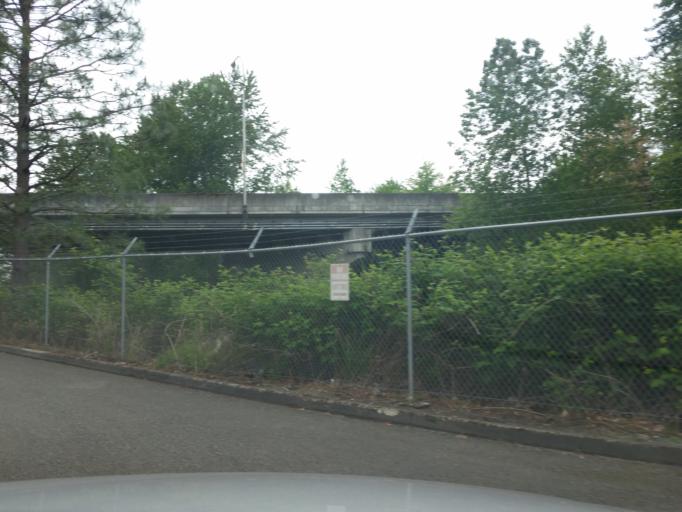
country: US
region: Washington
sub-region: King County
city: Bellevue
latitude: 47.6226
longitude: -122.1823
